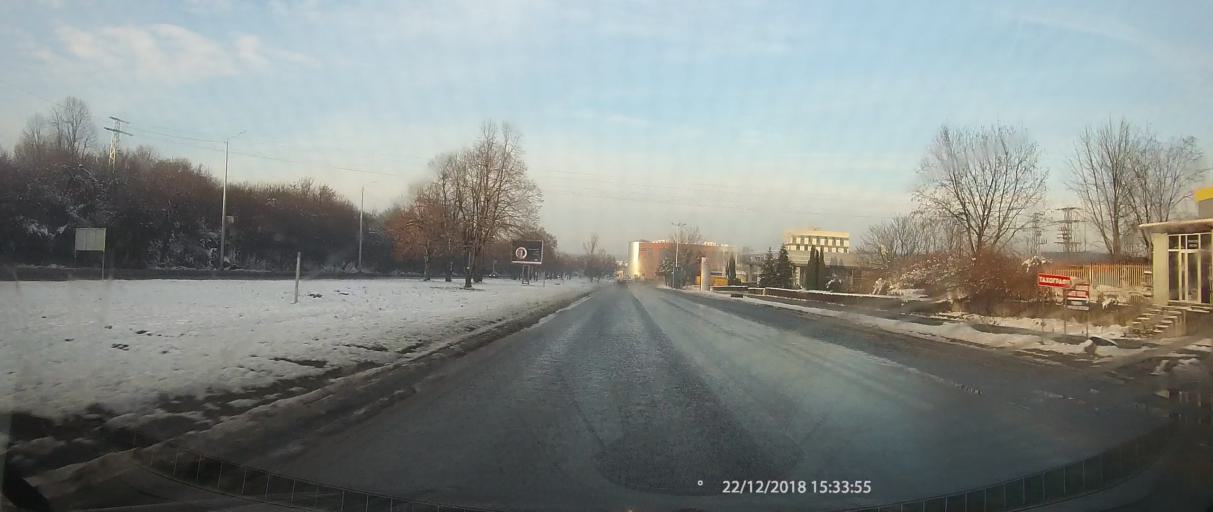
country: BG
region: Ruse
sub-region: Obshtina Ruse
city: Ruse
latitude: 43.8697
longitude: 26.0159
